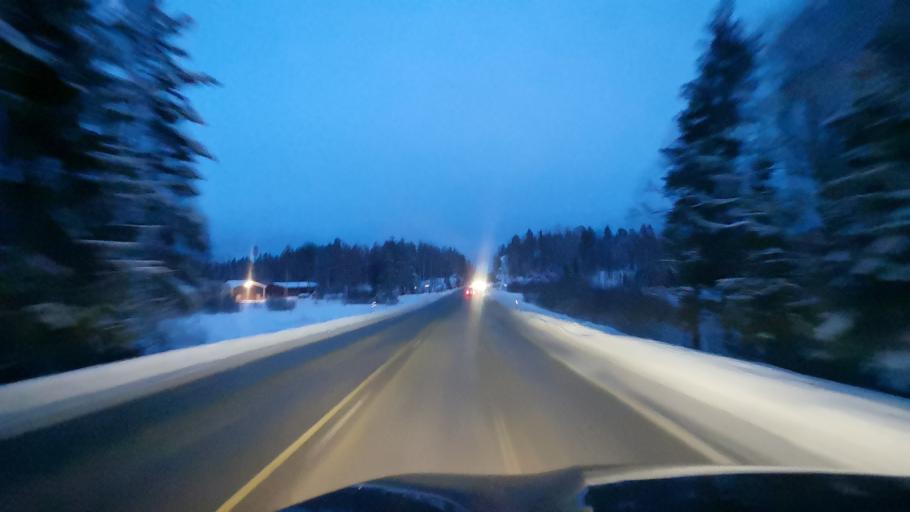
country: FI
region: Varsinais-Suomi
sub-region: Loimaa
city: Loimaa
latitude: 60.8730
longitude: 23.0646
